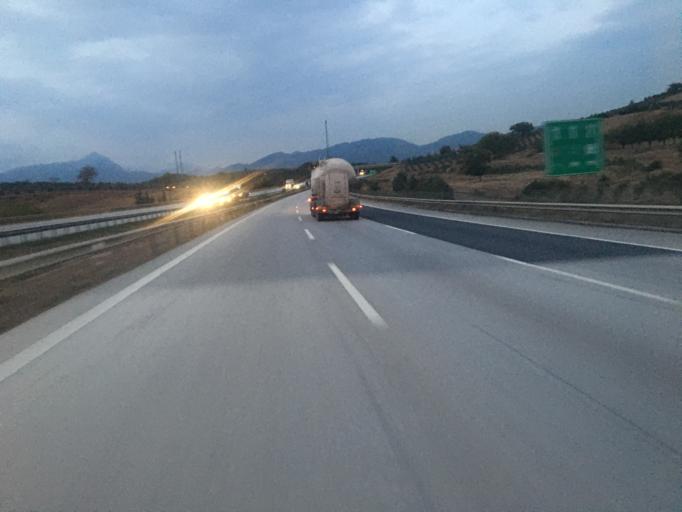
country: TR
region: Osmaniye
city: Haruniye
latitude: 37.1980
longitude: 36.3849
